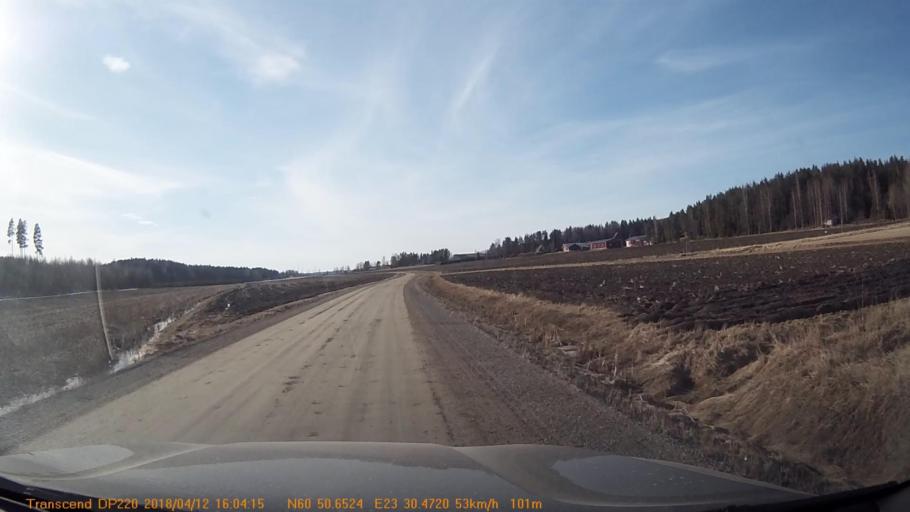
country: FI
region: Haeme
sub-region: Forssa
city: Jokioinen
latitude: 60.8443
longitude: 23.5076
